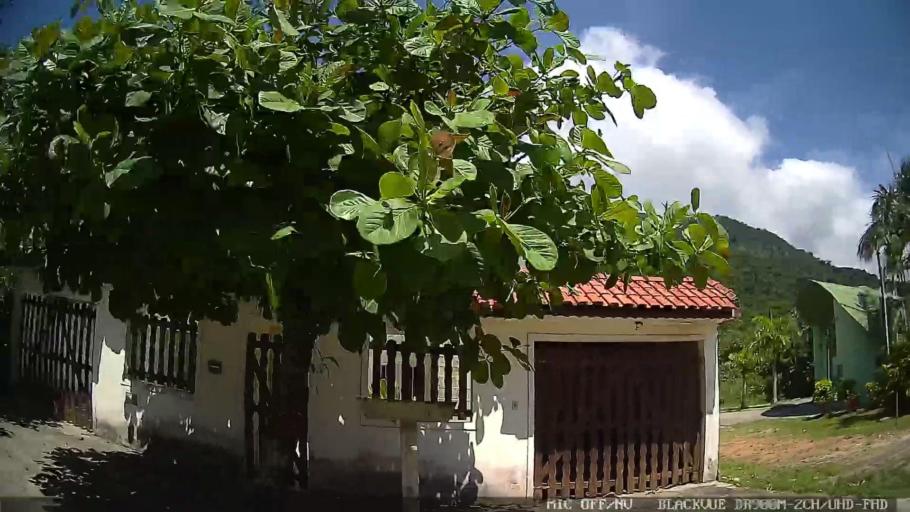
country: BR
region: Sao Paulo
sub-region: Peruibe
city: Peruibe
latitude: -24.3338
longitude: -47.0051
